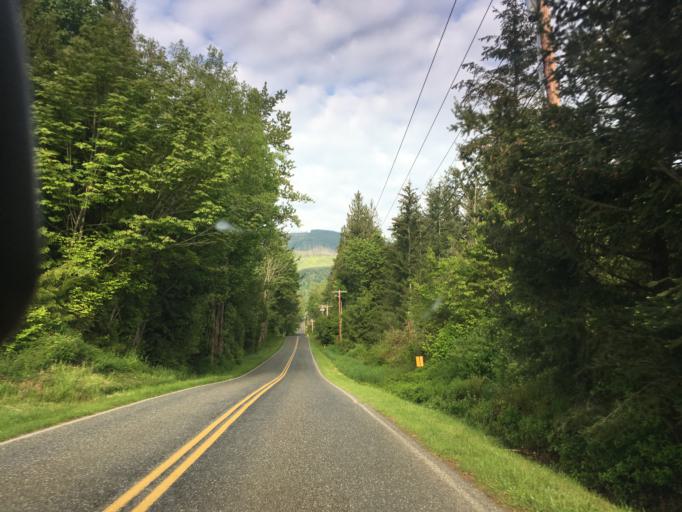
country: US
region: Washington
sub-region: Whatcom County
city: Sudden Valley
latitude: 48.7748
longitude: -122.3519
